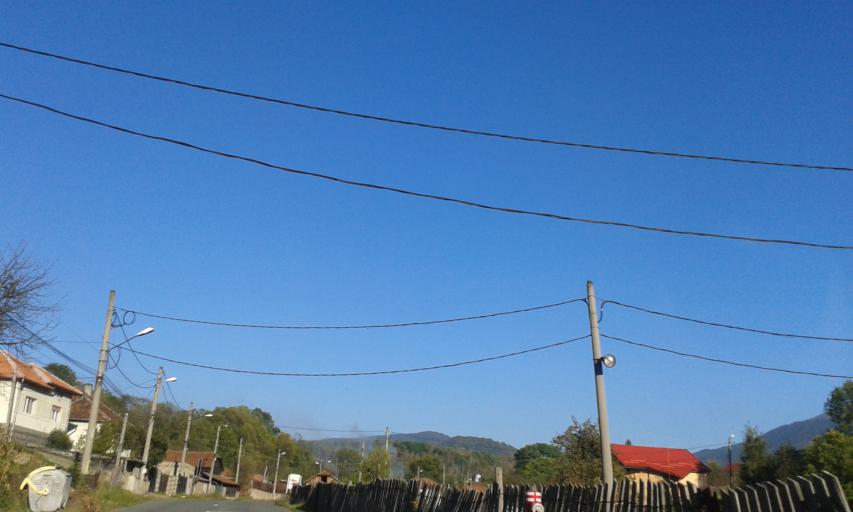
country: RO
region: Hunedoara
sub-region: Municipiul Petrosani
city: Petrosani
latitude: 45.4273
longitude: 23.3878
